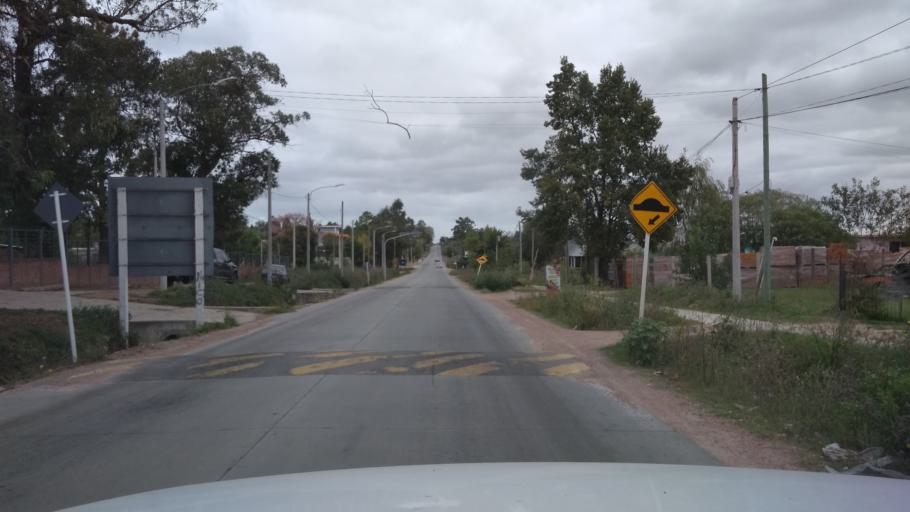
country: UY
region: Canelones
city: Toledo
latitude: -34.7822
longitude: -56.1375
